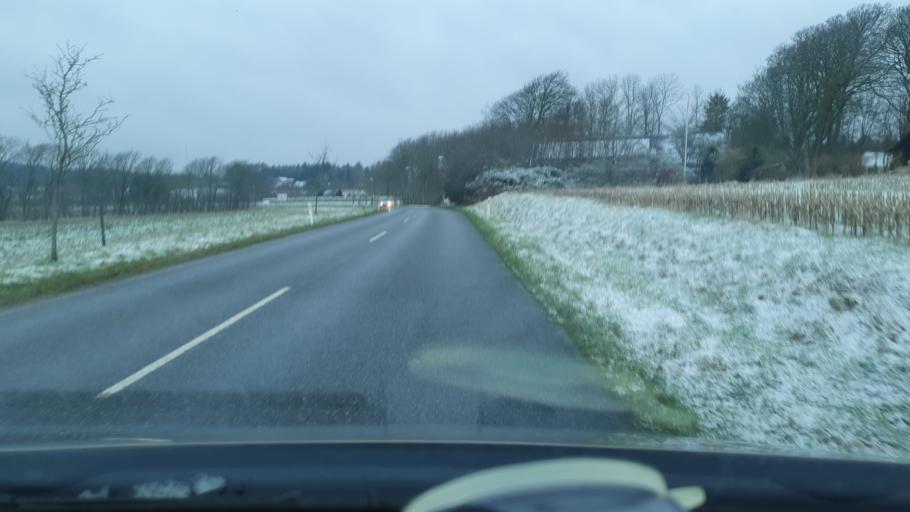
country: DK
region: North Denmark
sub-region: Jammerbugt Kommune
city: Brovst
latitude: 57.1304
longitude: 9.4716
